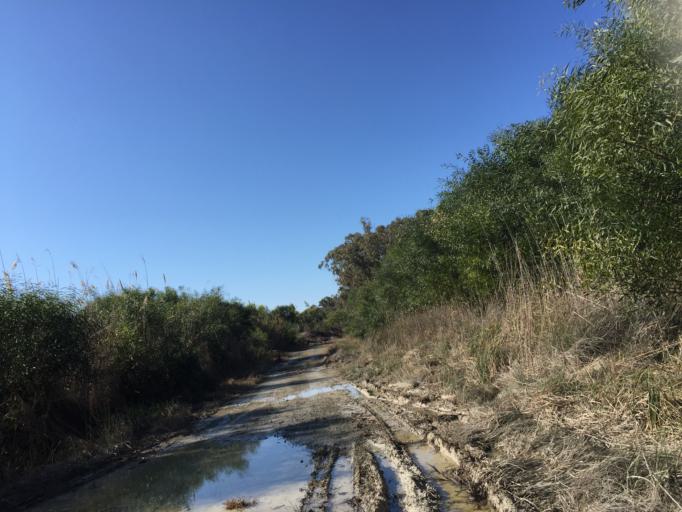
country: CY
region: Limassol
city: Ypsonas
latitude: 34.6404
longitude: 32.9773
